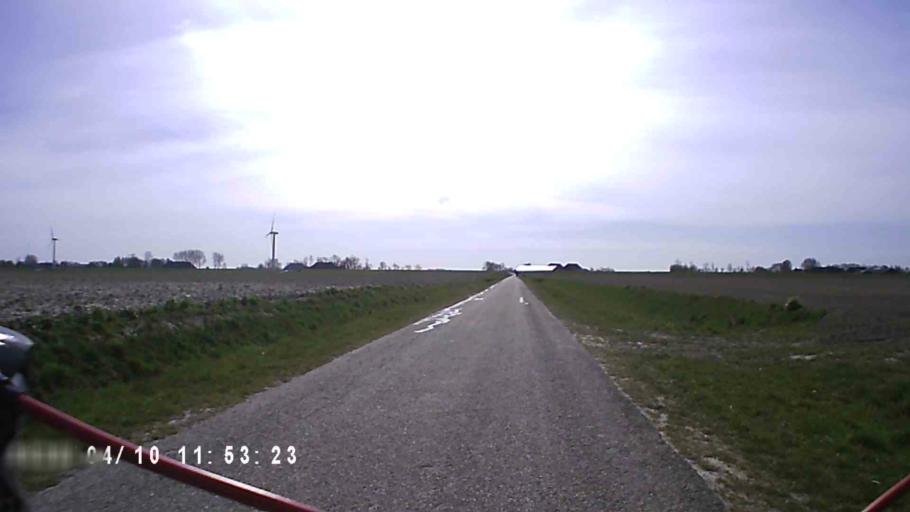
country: NL
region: Groningen
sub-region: Gemeente De Marne
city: Ulrum
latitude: 53.3915
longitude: 6.3326
